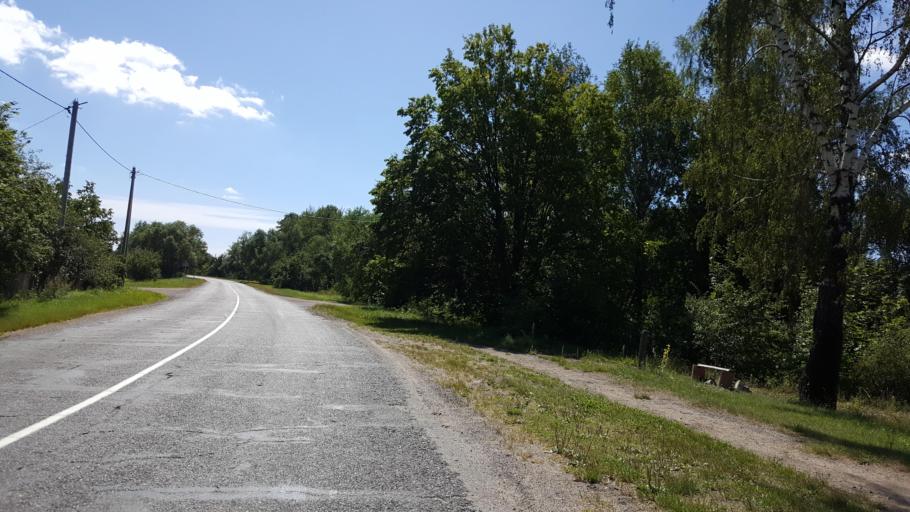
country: BY
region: Brest
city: Zhabinka
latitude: 52.3618
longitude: 24.1525
